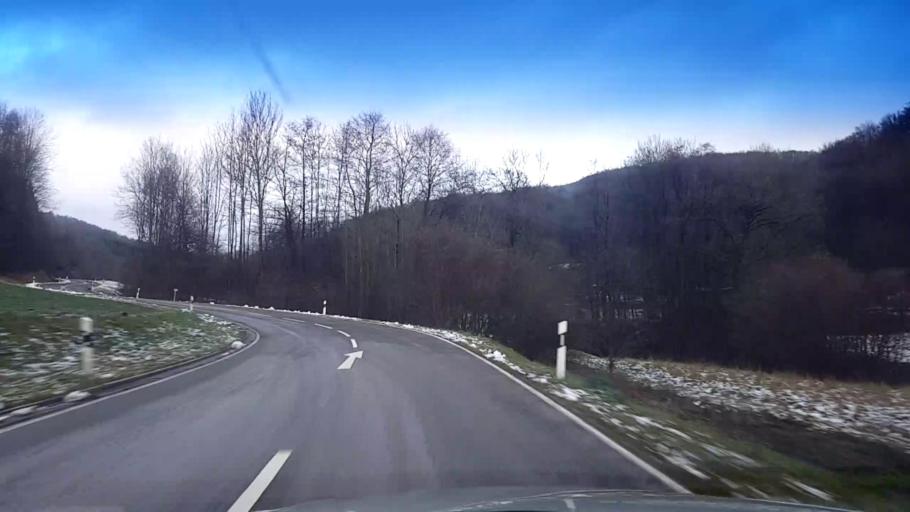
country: DE
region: Bavaria
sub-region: Upper Franconia
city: Buttenheim
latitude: 49.8356
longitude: 11.0769
